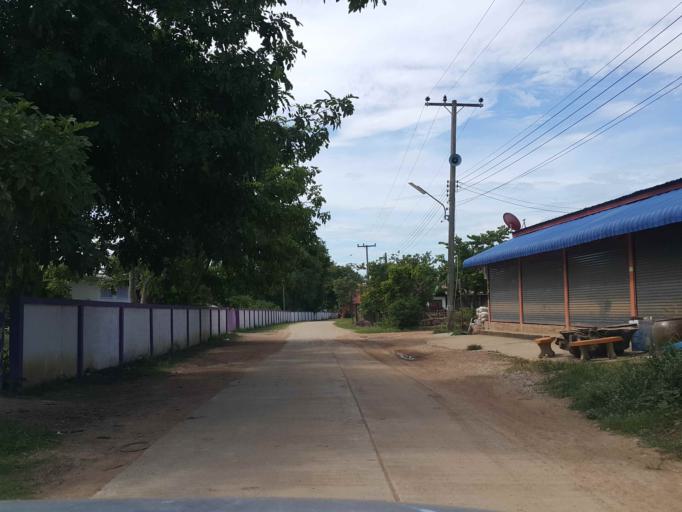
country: TH
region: Sukhothai
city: Ban Dan Lan Hoi
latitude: 17.1059
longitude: 99.4753
